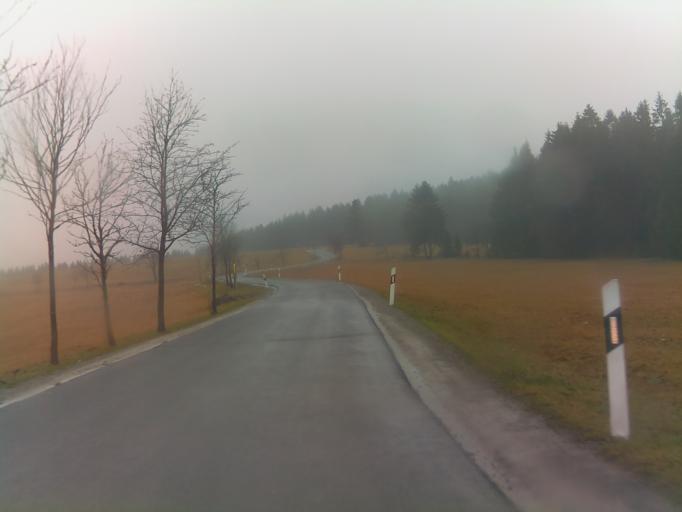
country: DE
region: Thuringia
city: Masserberg
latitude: 50.5156
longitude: 10.9336
